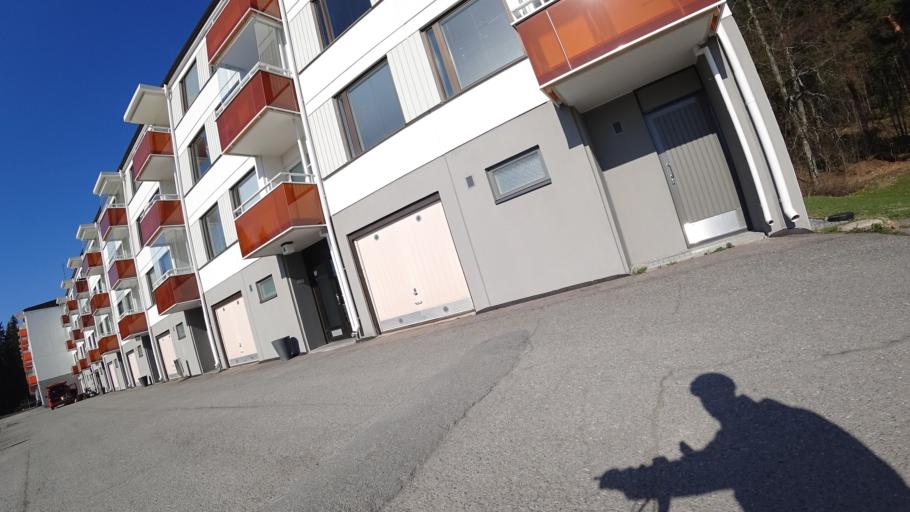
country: FI
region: Pirkanmaa
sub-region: Tampere
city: Pirkkala
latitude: 61.5042
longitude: 23.6366
